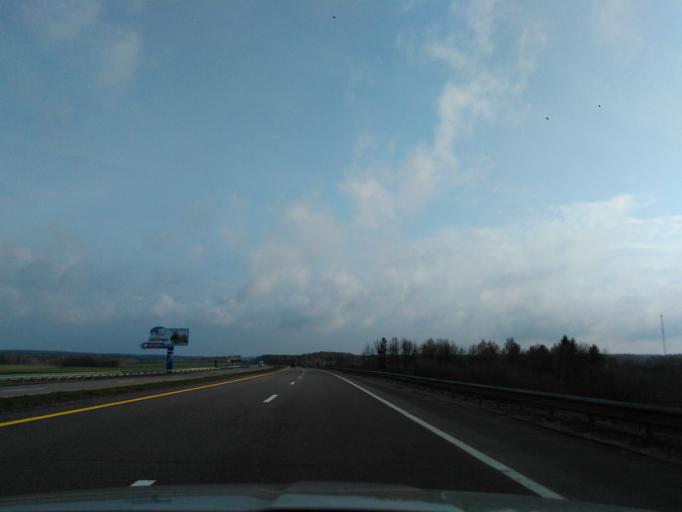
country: BY
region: Minsk
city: Lahoysk
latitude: 54.1550
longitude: 27.8110
